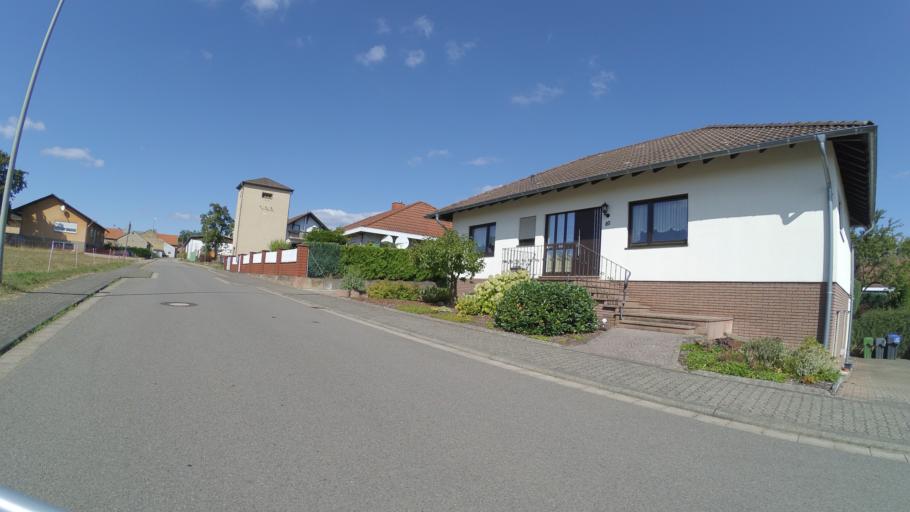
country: DE
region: Saarland
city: Lebach
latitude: 49.4180
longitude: 6.9027
